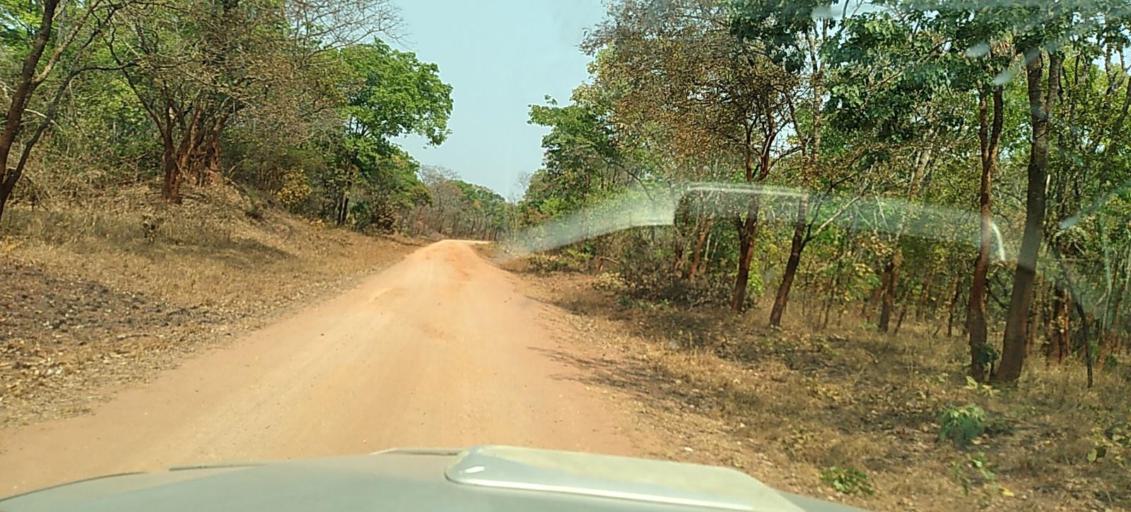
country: ZM
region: North-Western
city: Kasempa
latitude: -13.6847
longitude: 26.3186
